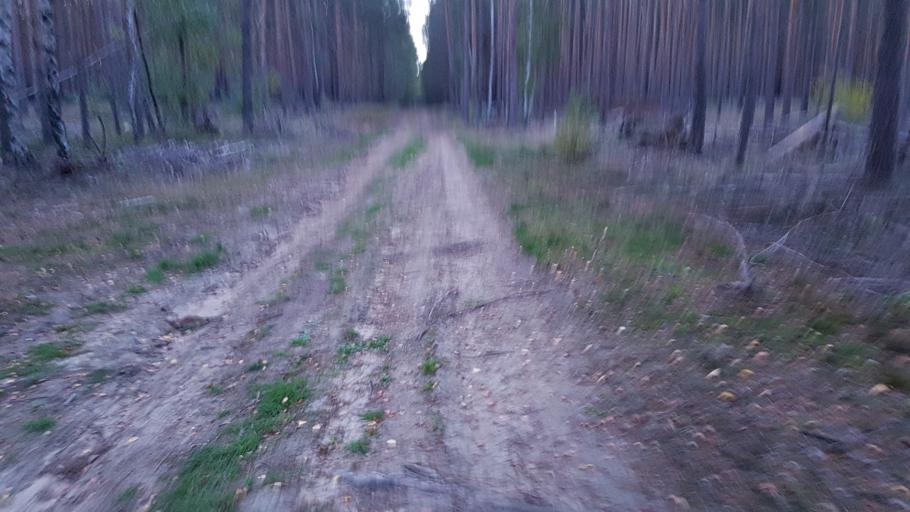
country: DE
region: Brandenburg
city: Trobitz
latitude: 51.5562
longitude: 13.4461
